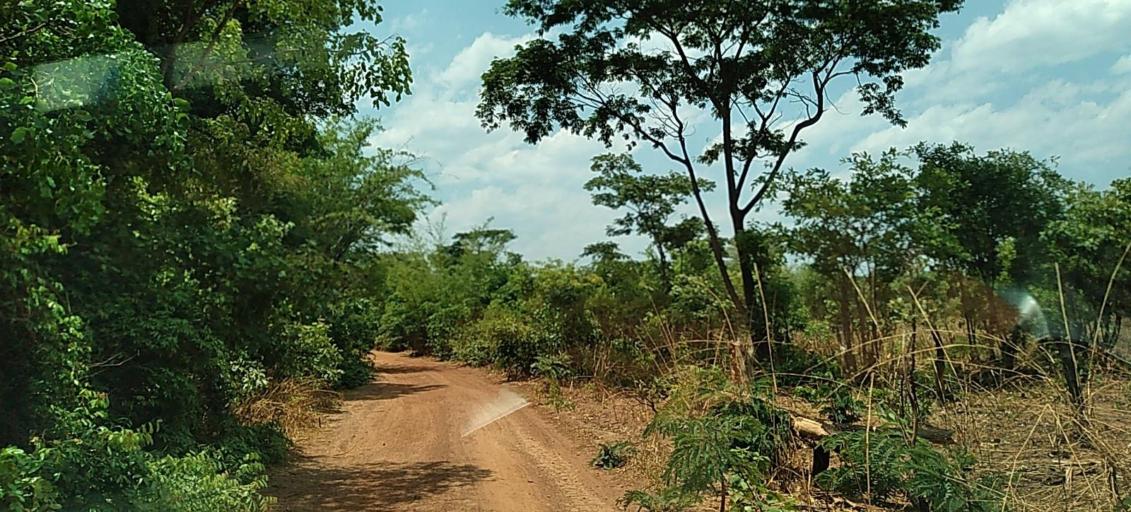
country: ZM
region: Copperbelt
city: Chingola
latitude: -12.5375
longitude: 27.6327
